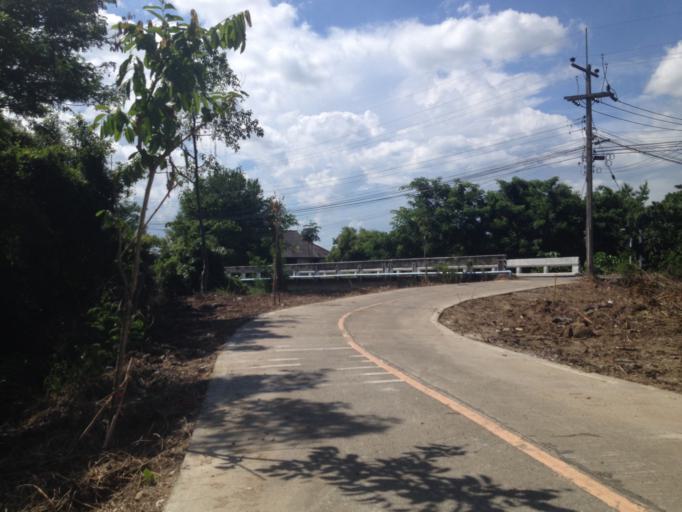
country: TH
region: Chiang Mai
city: Saraphi
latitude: 18.6998
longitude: 98.9796
